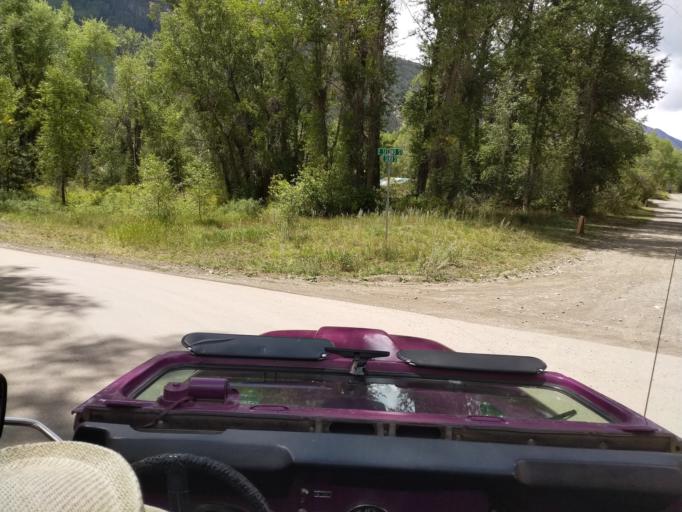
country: US
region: Colorado
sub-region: Gunnison County
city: Crested Butte
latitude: 39.0726
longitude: -107.1842
